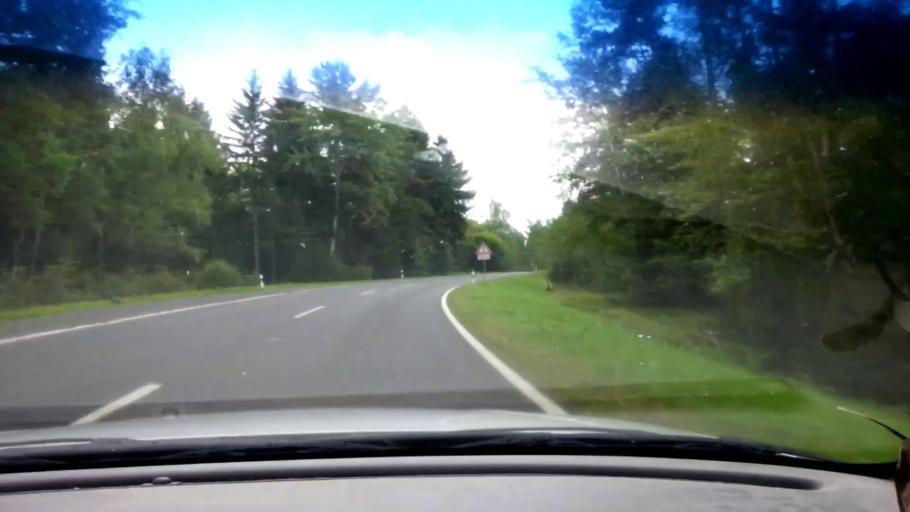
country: DE
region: Bavaria
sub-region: Upper Franconia
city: Schirnding
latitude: 50.0726
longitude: 12.2397
